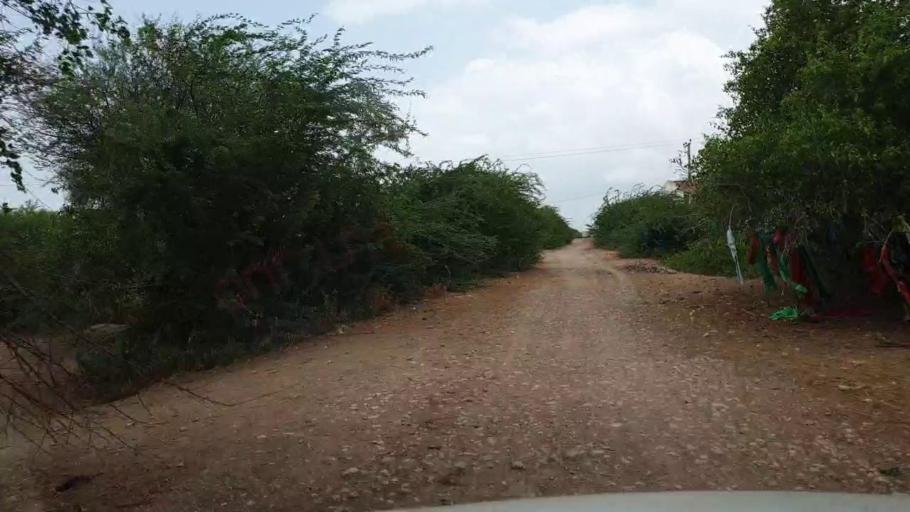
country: PK
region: Sindh
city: Kario
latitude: 24.6906
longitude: 68.6647
